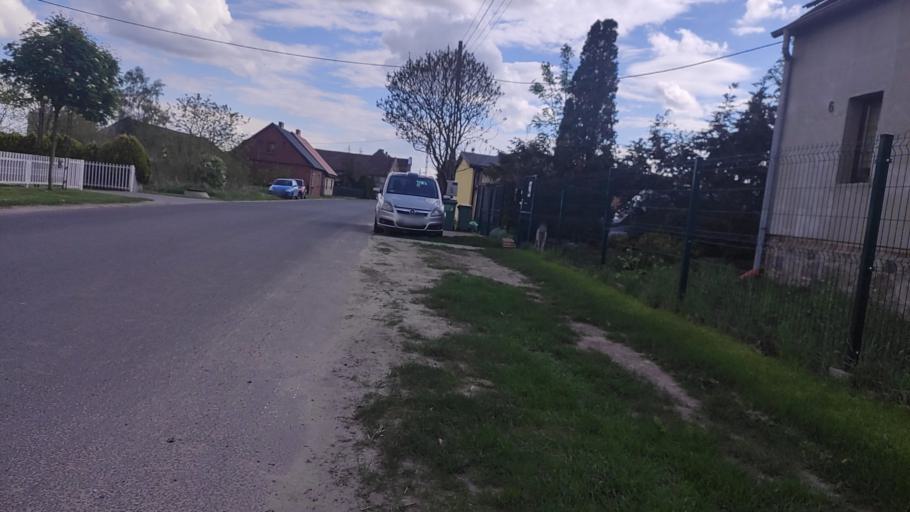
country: PL
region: Greater Poland Voivodeship
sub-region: Powiat poznanski
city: Kostrzyn
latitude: 52.4138
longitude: 17.1715
